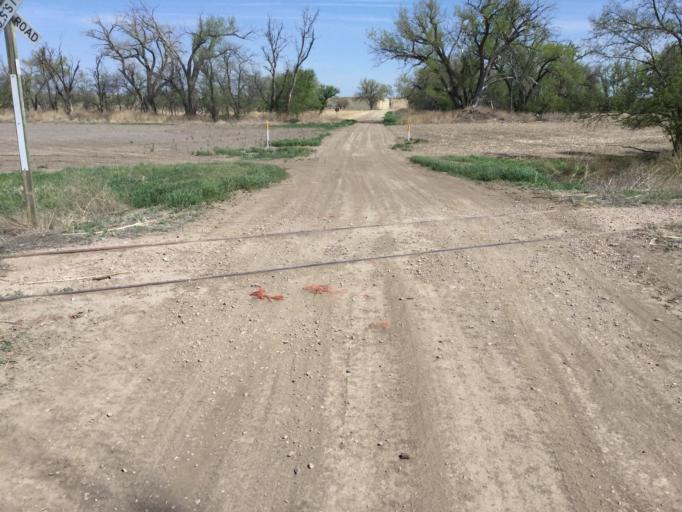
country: US
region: Kansas
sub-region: Decatur County
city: Oberlin
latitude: 39.9332
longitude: -100.6458
